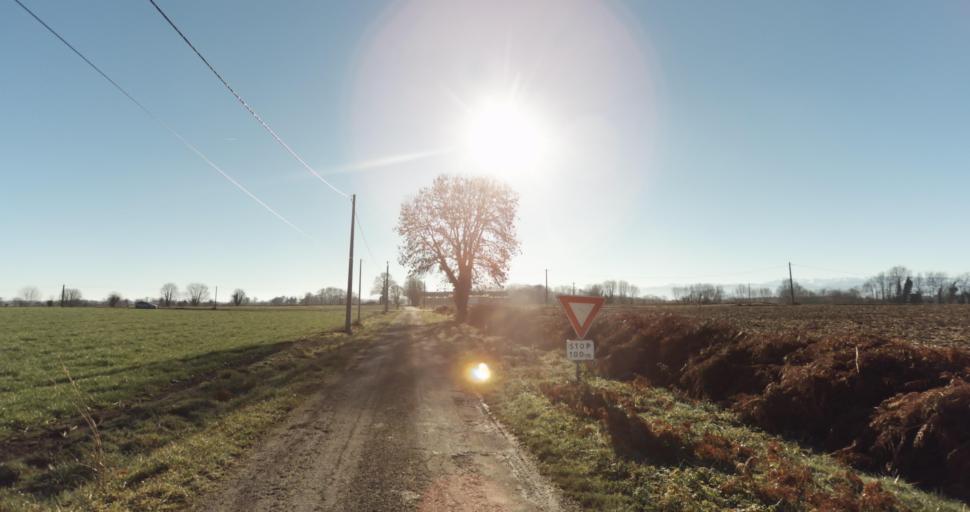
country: FR
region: Aquitaine
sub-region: Departement des Pyrenees-Atlantiques
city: Morlaas
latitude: 43.3401
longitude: -0.2356
